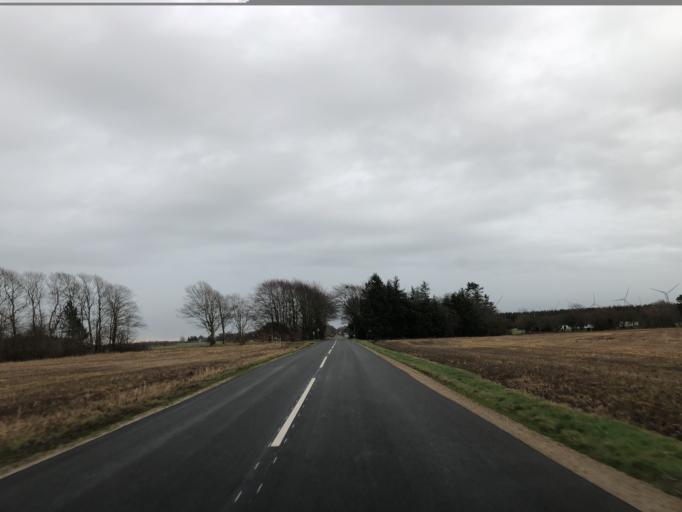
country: DK
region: Central Jutland
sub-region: Holstebro Kommune
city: Vinderup
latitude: 56.3785
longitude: 8.8471
